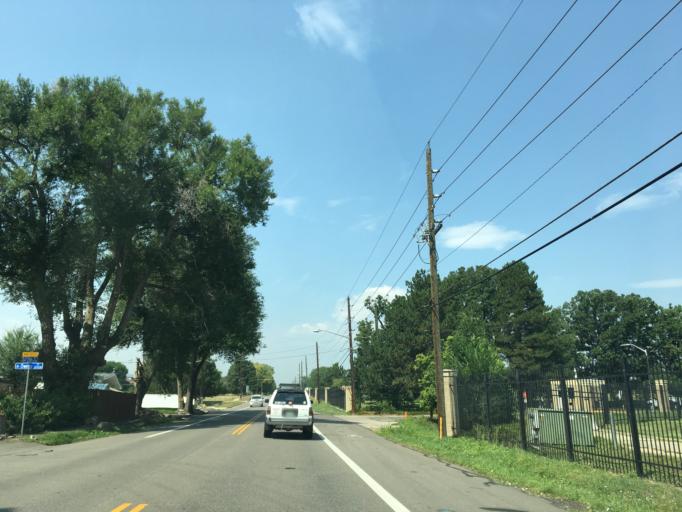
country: US
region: Colorado
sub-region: Jefferson County
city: Applewood
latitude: 39.7475
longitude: -105.1202
